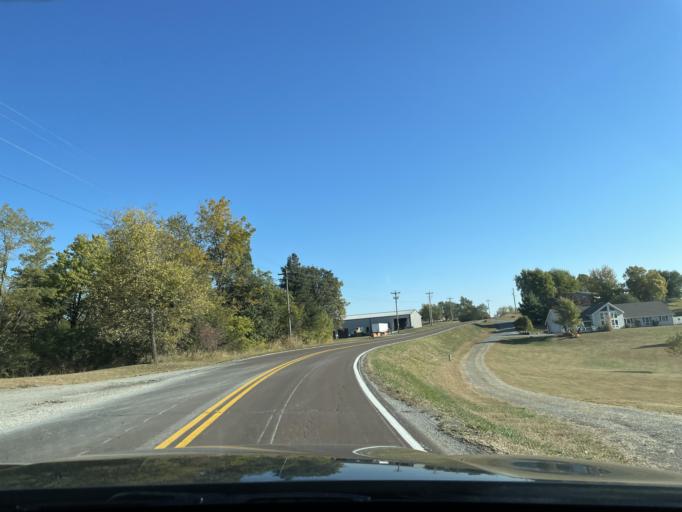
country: US
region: Missouri
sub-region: Andrew County
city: Savannah
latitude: 39.9157
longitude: -94.8758
